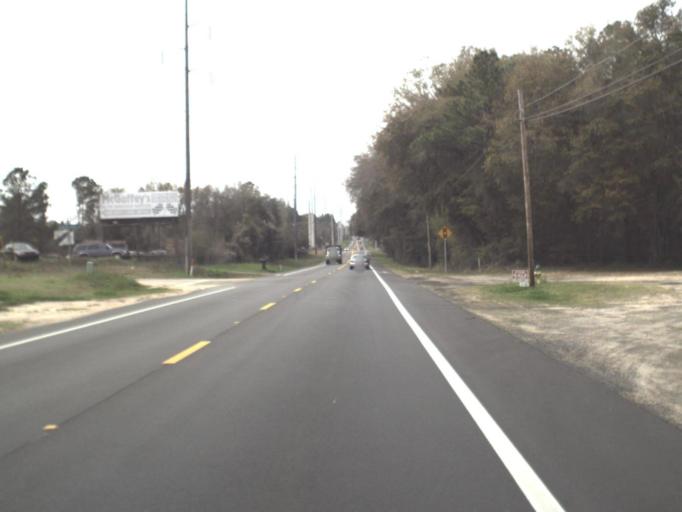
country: US
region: Florida
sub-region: Leon County
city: Tallahassee
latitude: 30.4354
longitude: -84.3691
